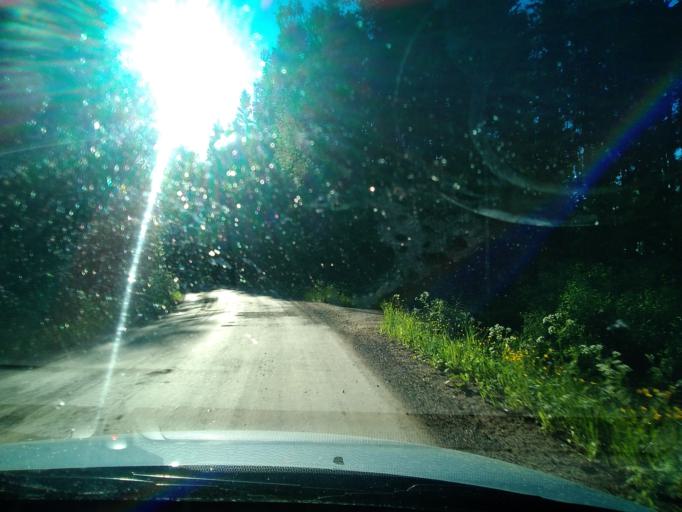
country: FI
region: Haeme
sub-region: Forssa
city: Tammela
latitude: 60.7611
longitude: 23.7960
